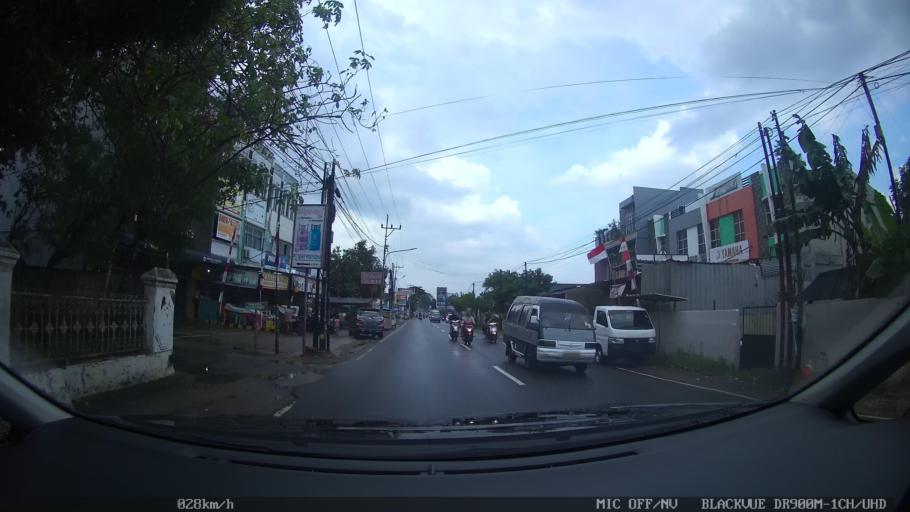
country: ID
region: Lampung
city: Kedaton
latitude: -5.3859
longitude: 105.2931
